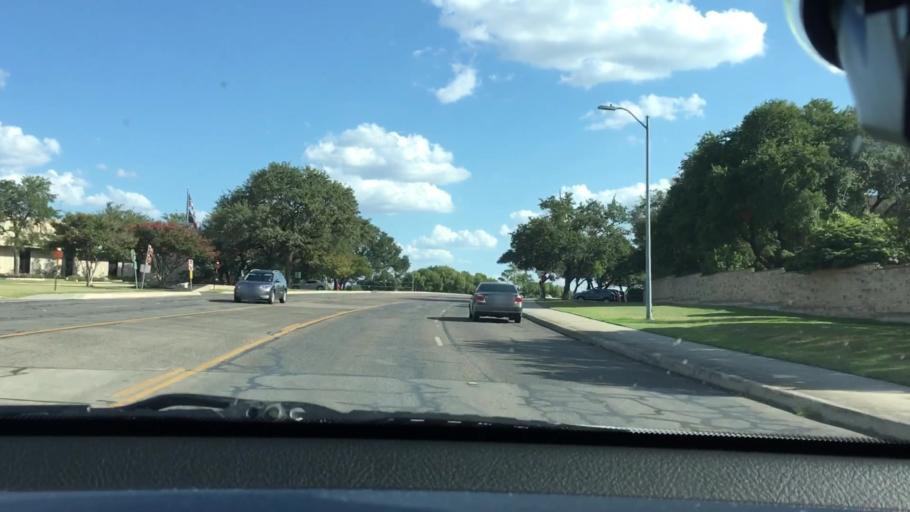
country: US
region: Texas
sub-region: Bexar County
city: Universal City
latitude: 29.5577
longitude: -98.3087
